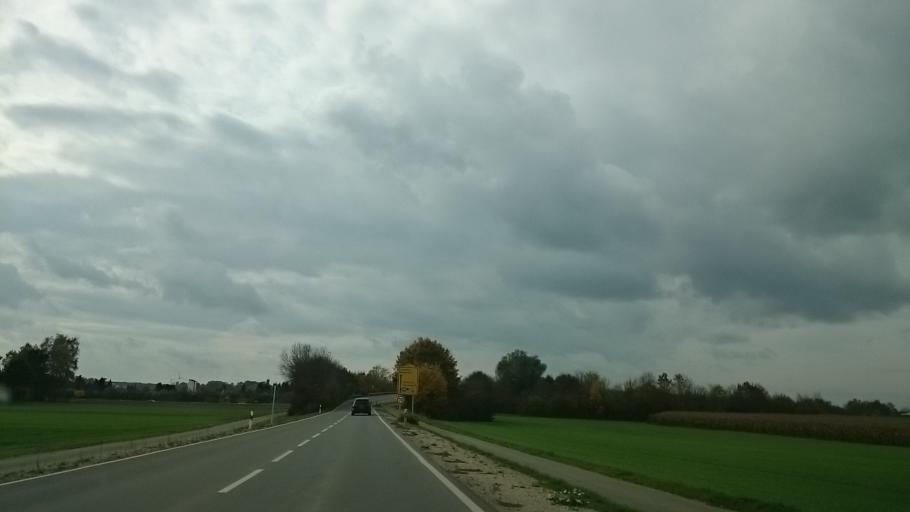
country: DE
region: Bavaria
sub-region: Swabia
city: Nordendorf
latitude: 48.5950
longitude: 10.8447
